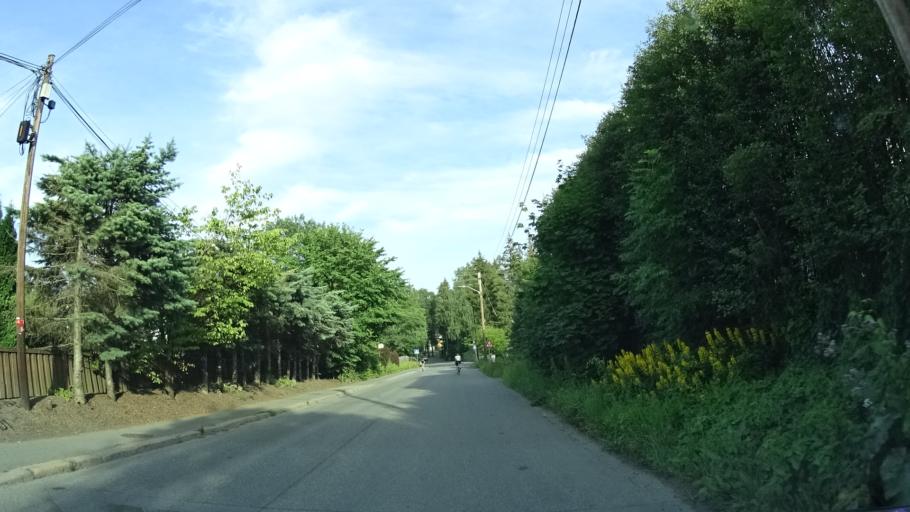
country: NO
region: Oslo
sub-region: Oslo
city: Sjolyststranda
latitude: 59.9513
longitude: 10.6772
